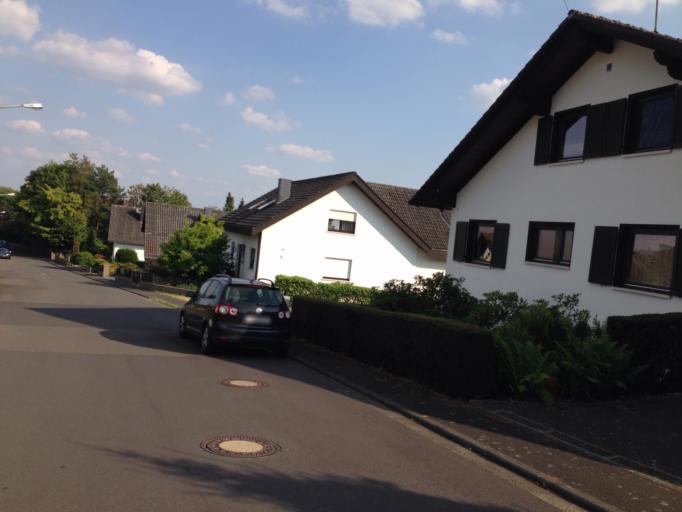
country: DE
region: Hesse
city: Lollar
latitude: 50.6409
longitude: 8.6581
